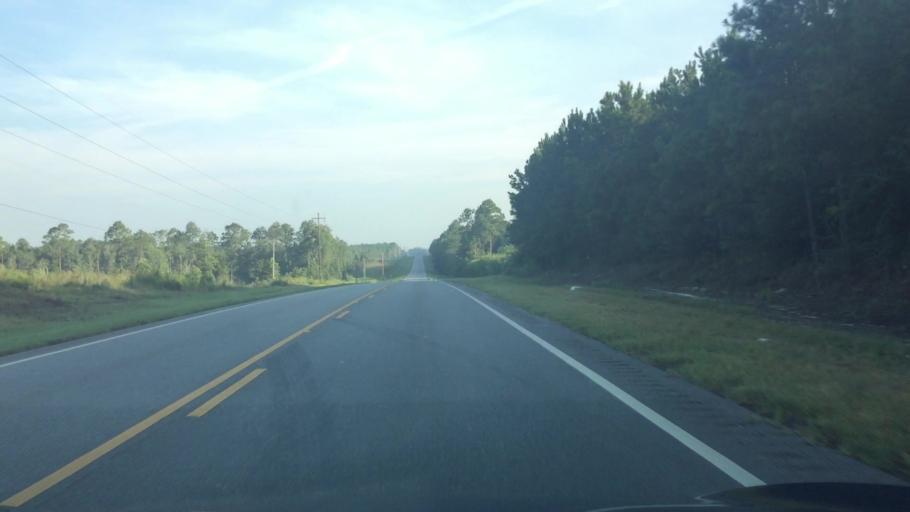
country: US
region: Alabama
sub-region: Covington County
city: Florala
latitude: 31.0336
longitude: -86.3741
